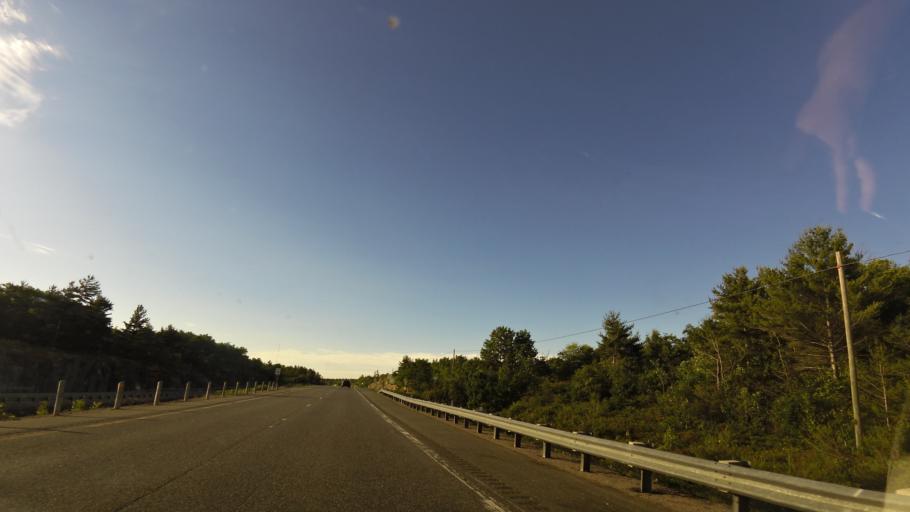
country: CA
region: Ontario
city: Midland
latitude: 44.9253
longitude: -79.7748
